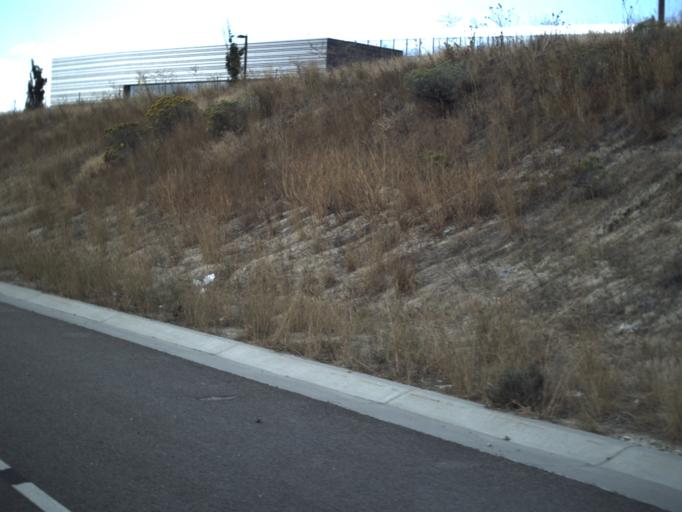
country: US
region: Utah
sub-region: Utah County
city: Lehi
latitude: 40.4326
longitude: -111.8908
